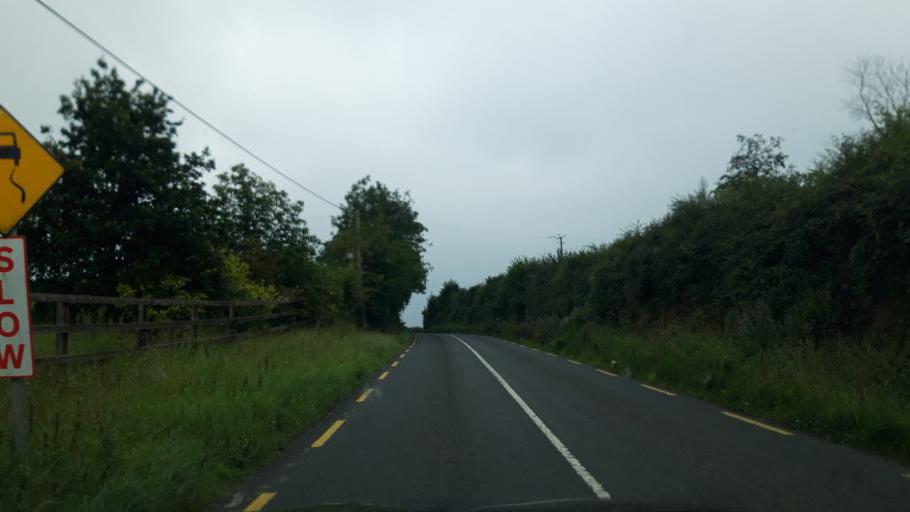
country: IE
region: Munster
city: Fethard
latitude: 52.4525
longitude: -7.7038
